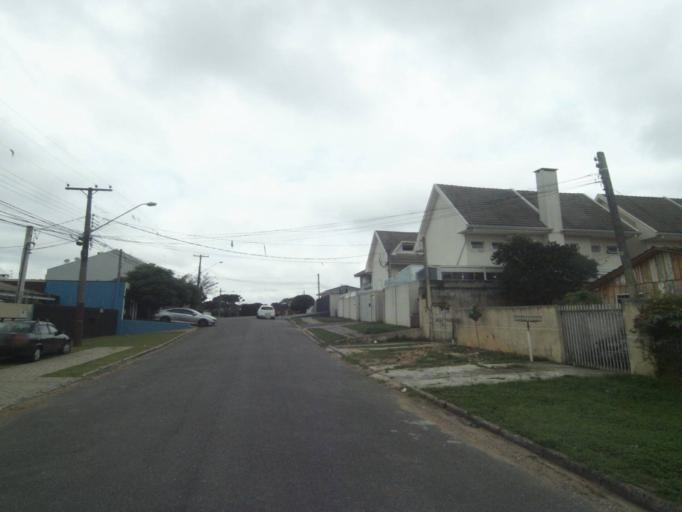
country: BR
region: Parana
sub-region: Sao Jose Dos Pinhais
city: Sao Jose dos Pinhais
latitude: -25.5450
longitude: -49.2828
